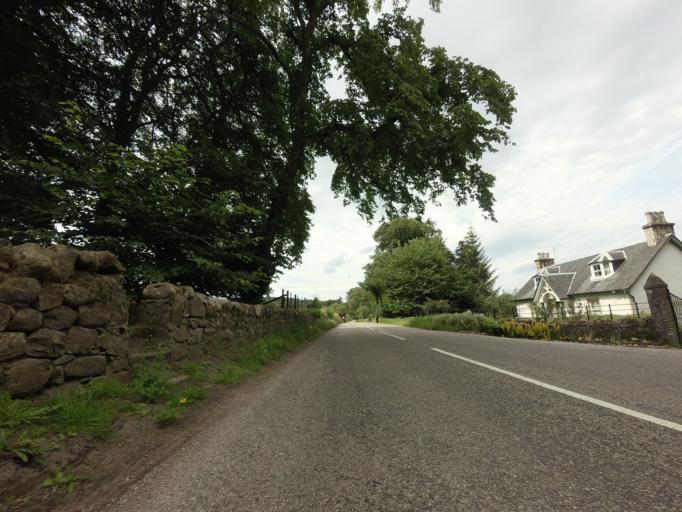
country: GB
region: Scotland
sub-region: Highland
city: Alness
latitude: 57.8552
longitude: -4.3077
